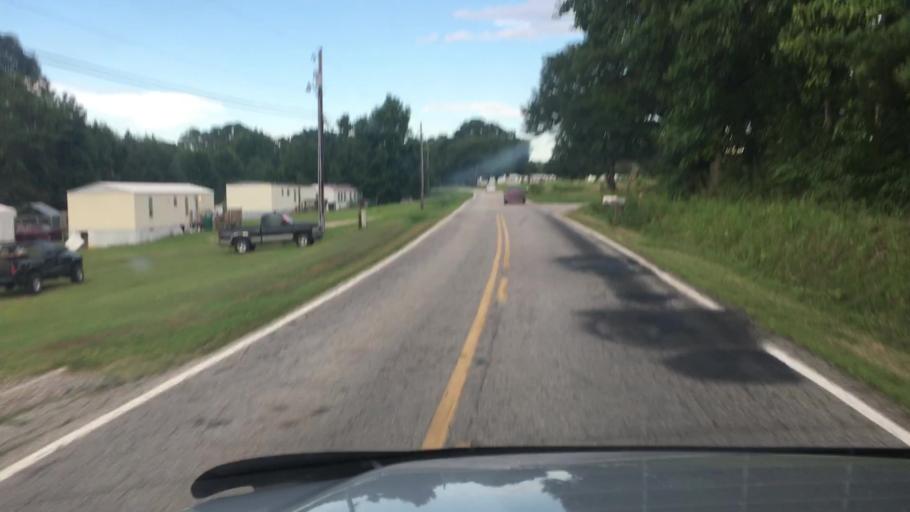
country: US
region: South Carolina
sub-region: Spartanburg County
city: Mayo
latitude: 35.1300
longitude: -81.8394
